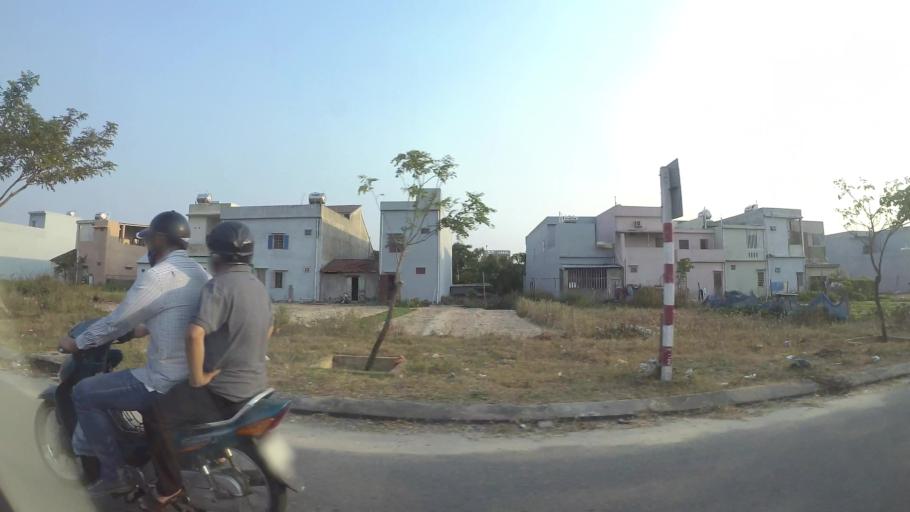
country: VN
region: Da Nang
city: Ngu Hanh Son
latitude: 15.9831
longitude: 108.2521
